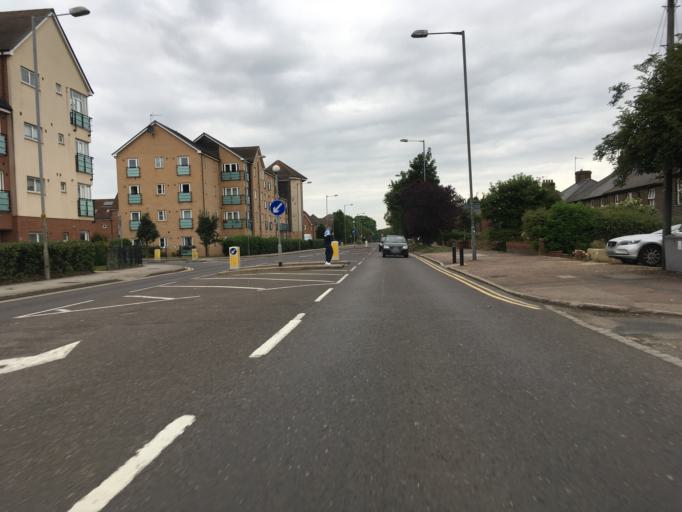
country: GB
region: England
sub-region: Central Bedfordshire
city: Dunstable
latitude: 51.8952
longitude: -0.5338
